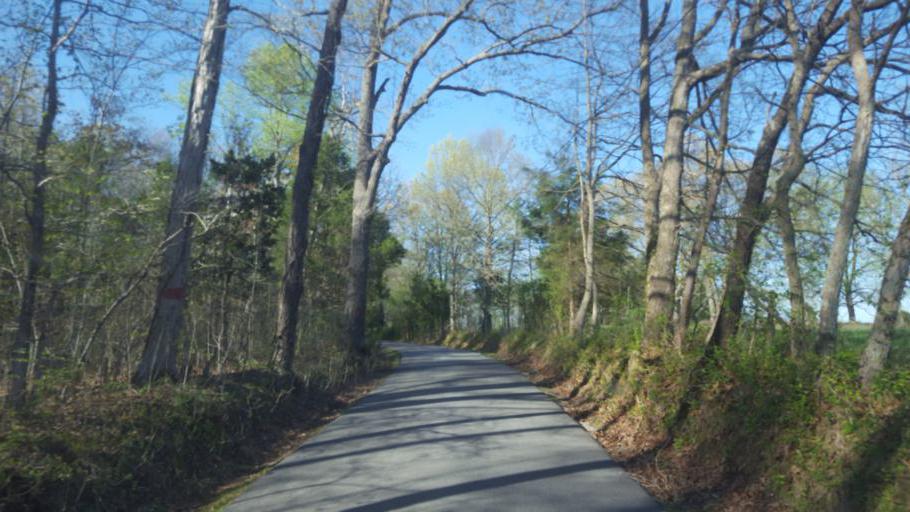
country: US
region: Kentucky
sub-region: Barren County
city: Cave City
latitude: 37.1931
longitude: -86.0468
